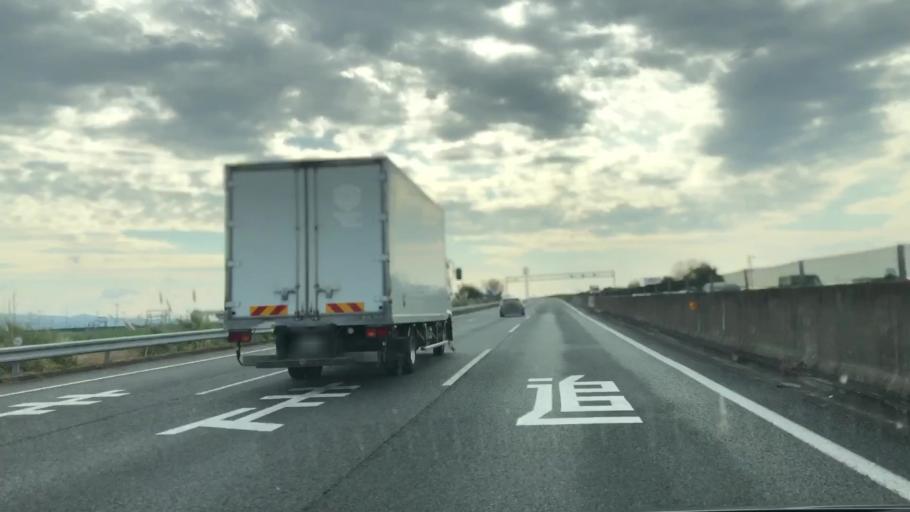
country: JP
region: Saga Prefecture
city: Tosu
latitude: 33.3588
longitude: 130.5397
